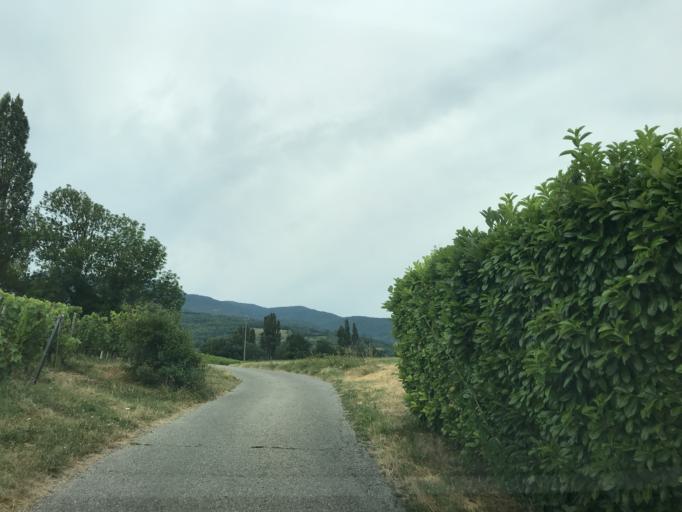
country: FR
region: Rhone-Alpes
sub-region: Departement de la Savoie
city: Les Marches
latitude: 45.4968
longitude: 5.9661
